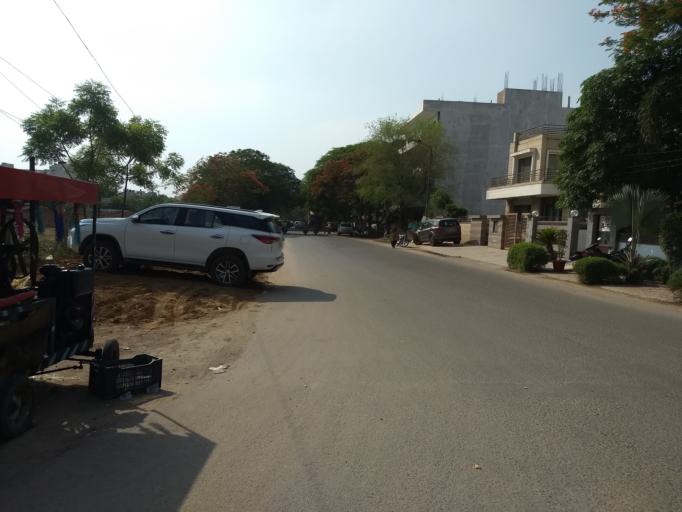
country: IN
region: Haryana
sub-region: Gurgaon
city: Gurgaon
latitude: 28.4453
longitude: 77.0630
